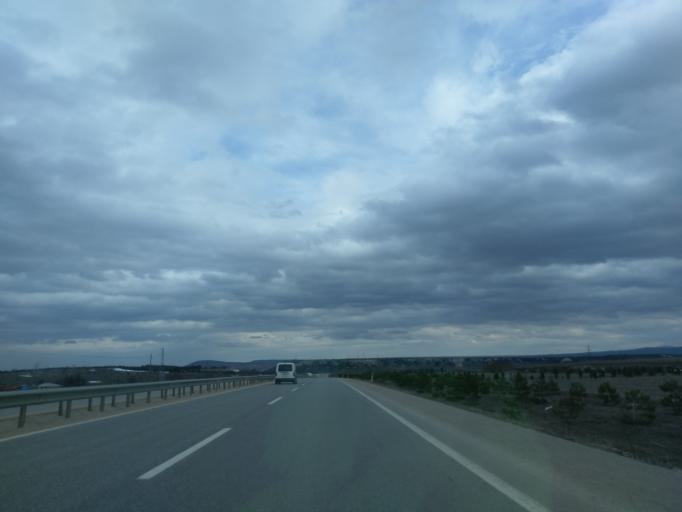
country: TR
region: Eskisehir
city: Inonu
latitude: 39.7254
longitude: 30.3203
